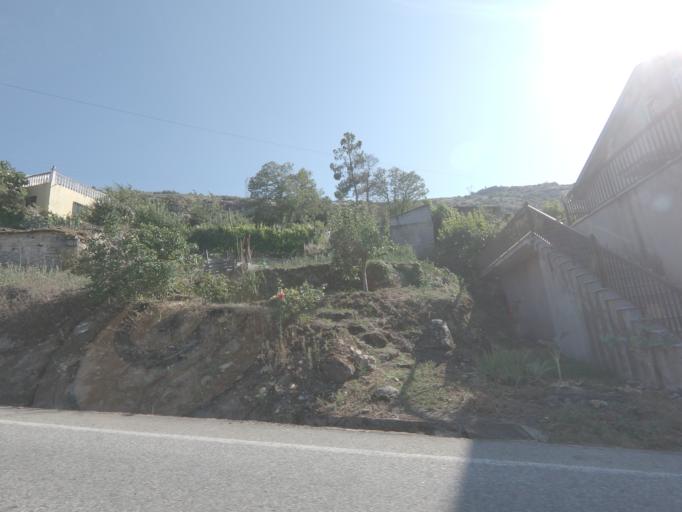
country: PT
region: Viseu
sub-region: Tabuaco
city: Tabuaco
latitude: 41.1144
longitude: -7.5699
